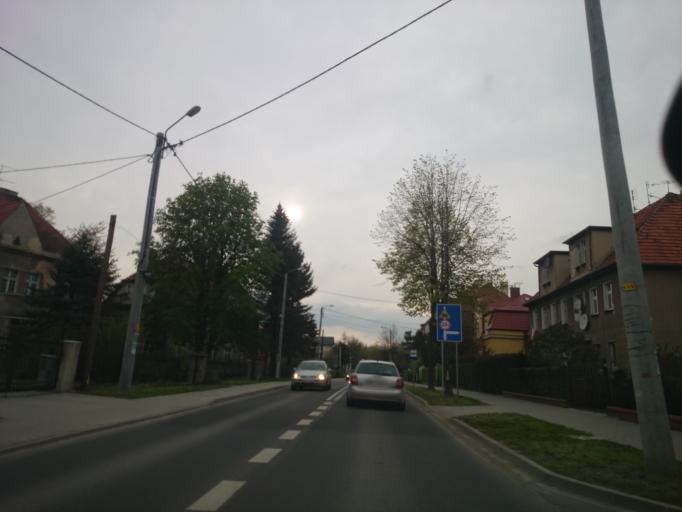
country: PL
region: Lower Silesian Voivodeship
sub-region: Powiat zabkowicki
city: Zabkowice Slaskie
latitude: 50.5880
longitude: 16.8225
